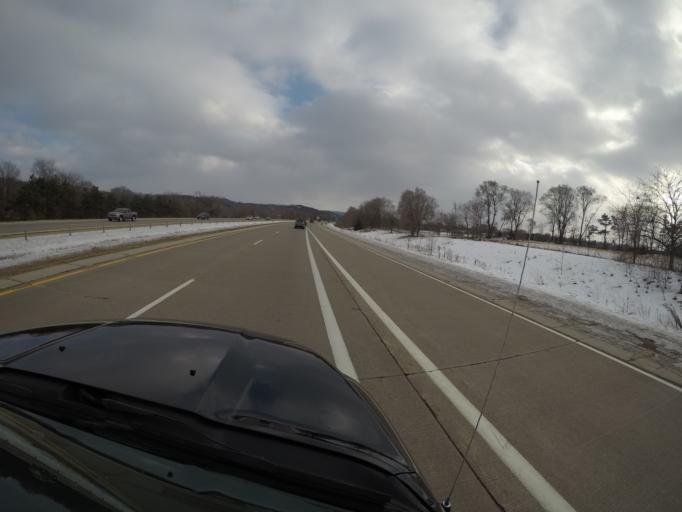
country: US
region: Wisconsin
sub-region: La Crosse County
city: Holmen
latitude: 43.9388
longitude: -91.2511
